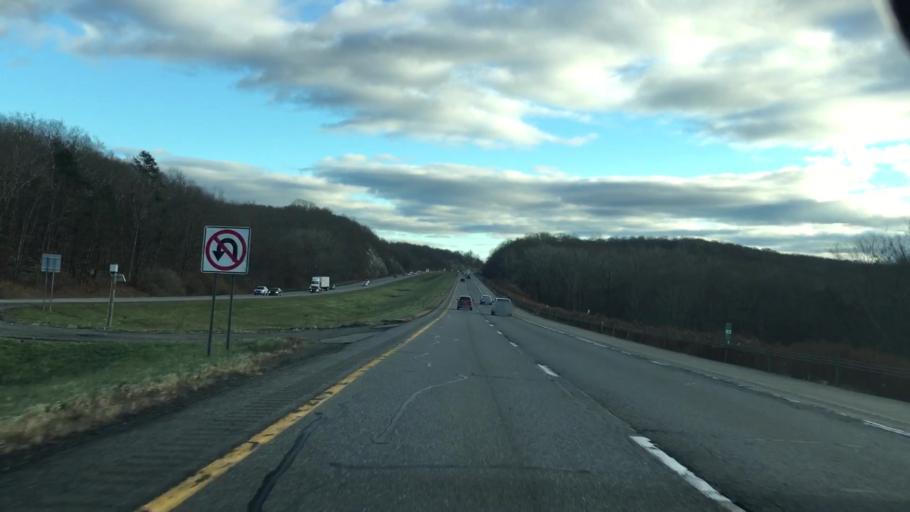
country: US
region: New York
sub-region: Putnam County
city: Lake Carmel
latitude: 41.4500
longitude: -73.6378
